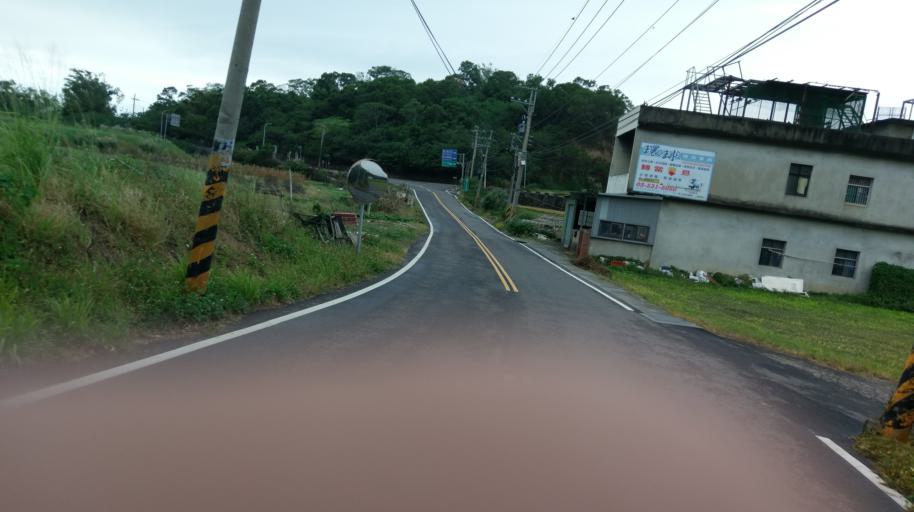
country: TW
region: Taiwan
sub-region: Hsinchu
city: Hsinchu
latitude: 24.7305
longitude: 120.9439
